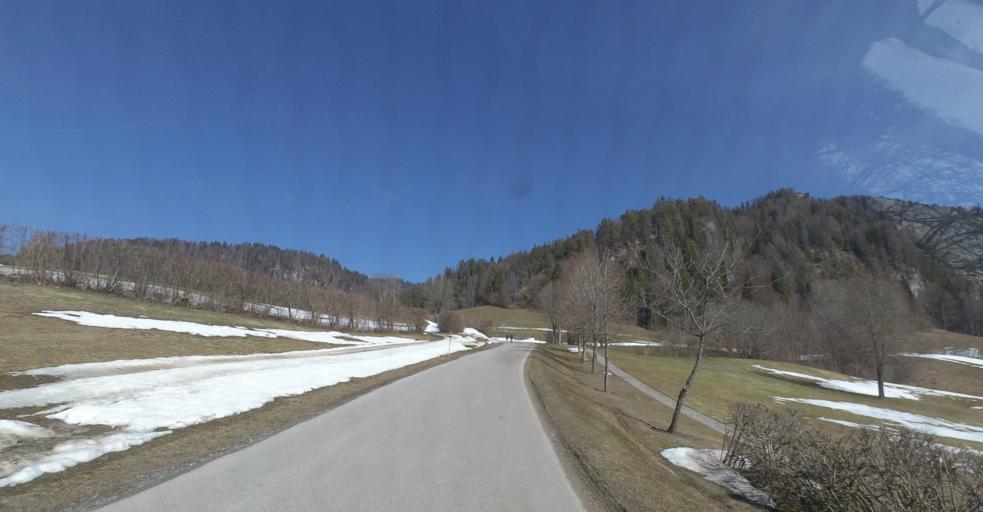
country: DE
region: Bavaria
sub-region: Upper Bavaria
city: Reit im Winkl
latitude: 47.6764
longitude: 12.4516
